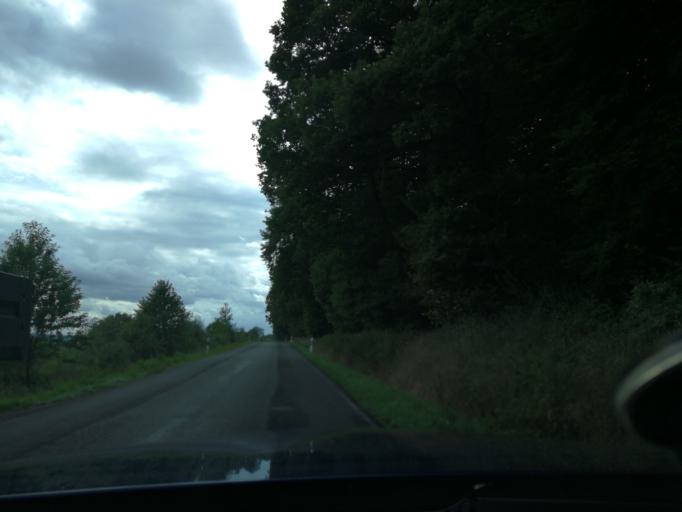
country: DE
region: Rheinland-Pfalz
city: Klausen
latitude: 49.9213
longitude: 6.8753
